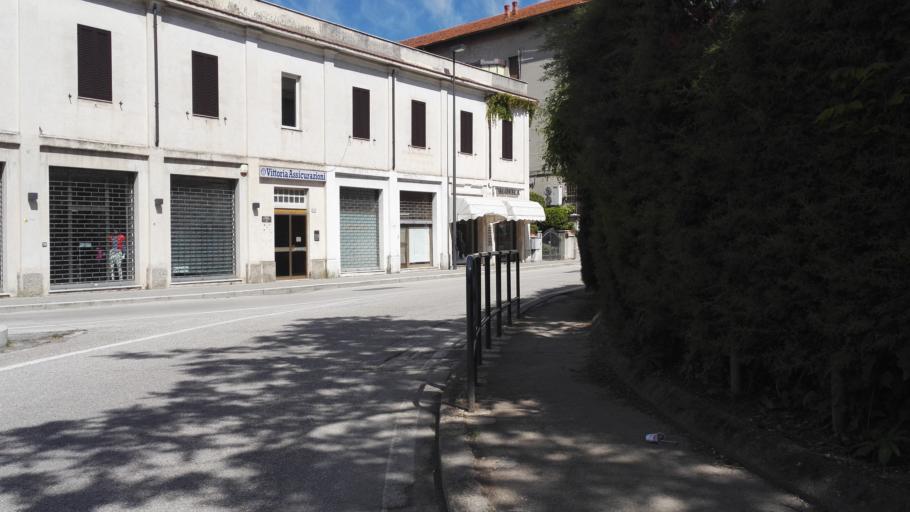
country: IT
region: Umbria
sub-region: Provincia di Perugia
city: Spoleto
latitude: 42.7406
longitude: 12.7361
